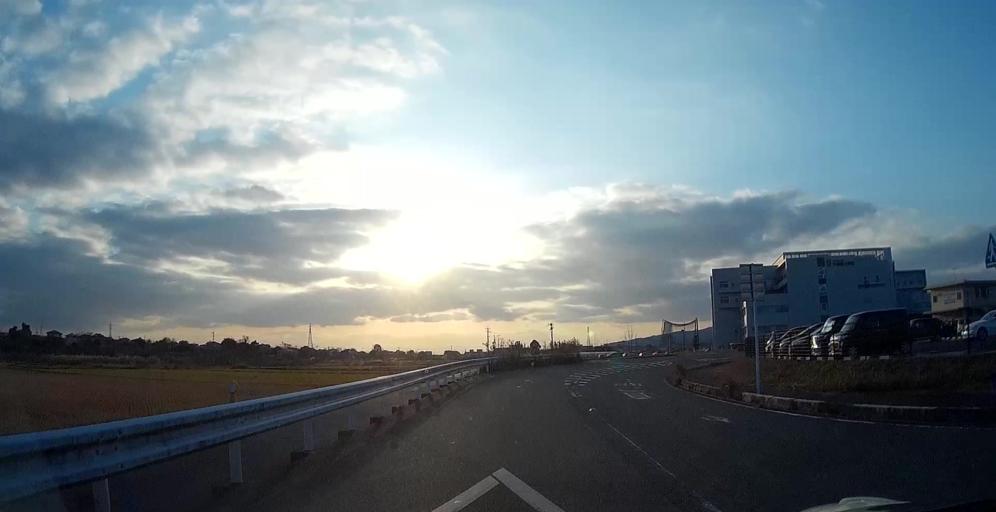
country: JP
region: Kumamoto
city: Matsubase
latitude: 32.6506
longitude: 130.6984
